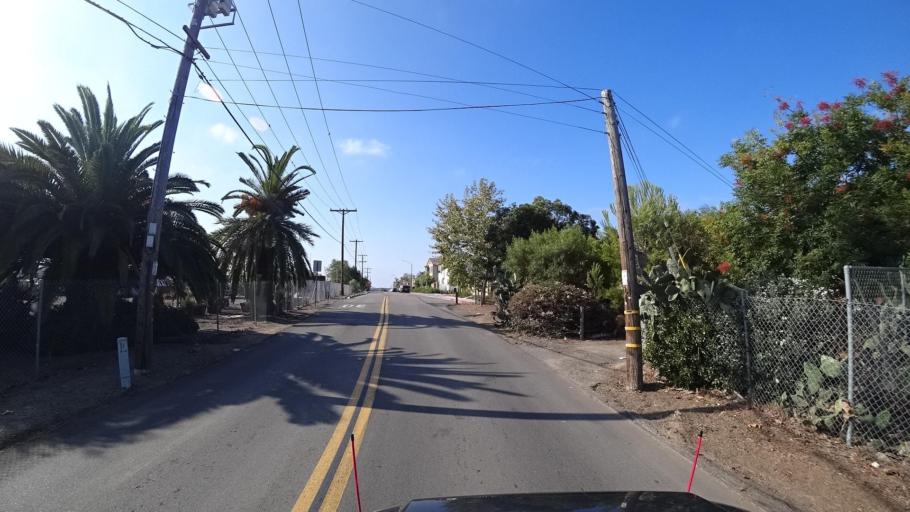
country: US
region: California
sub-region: San Diego County
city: Vista
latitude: 33.1706
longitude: -117.2464
